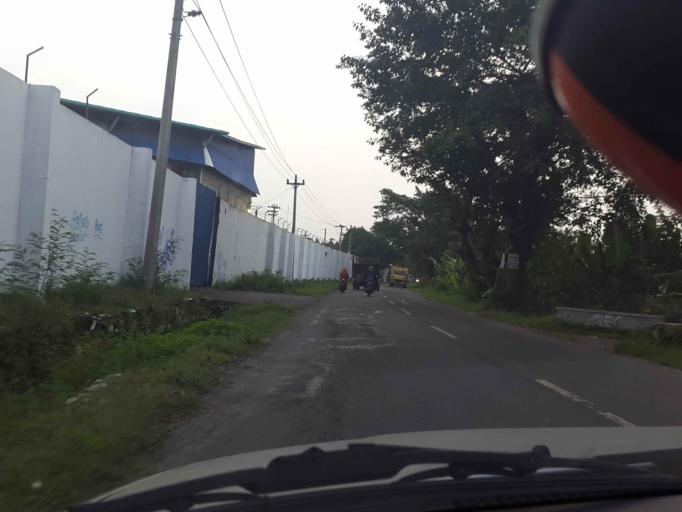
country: ID
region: Central Java
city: Jaten
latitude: -7.5483
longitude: 110.9130
